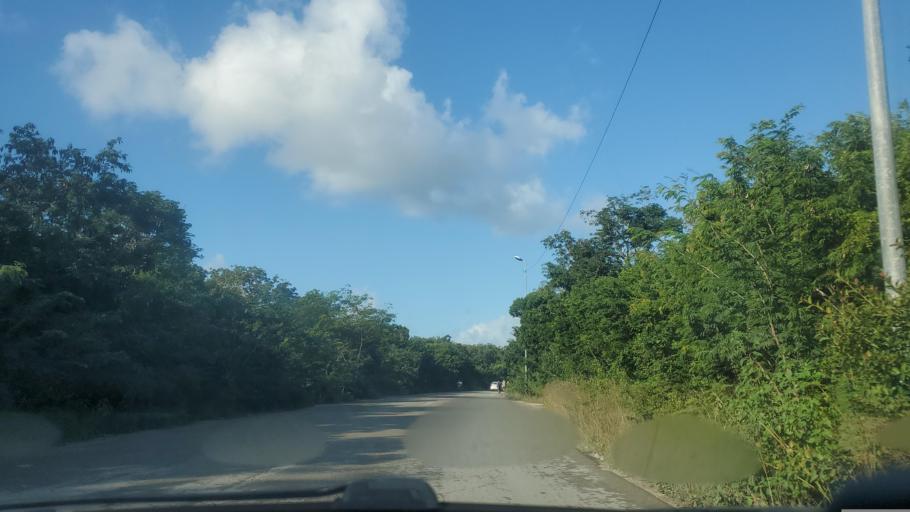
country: MX
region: Quintana Roo
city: Tulum
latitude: 20.2090
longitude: -87.4805
